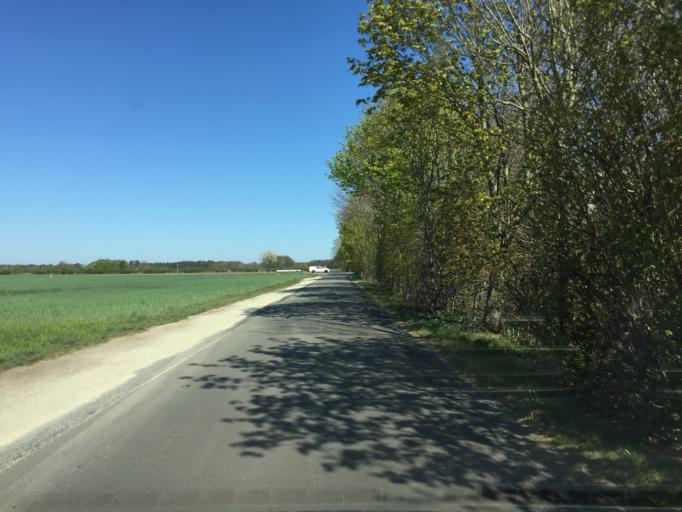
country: DE
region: Lower Saxony
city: Wehrbleck
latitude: 52.6278
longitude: 8.6868
